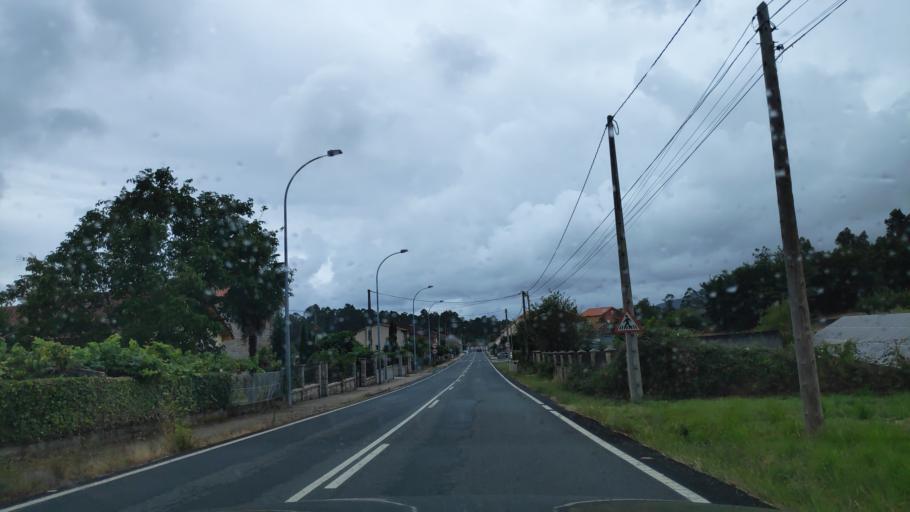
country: ES
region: Galicia
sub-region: Provincia de Pontevedra
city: Catoira
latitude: 42.6933
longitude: -8.7672
